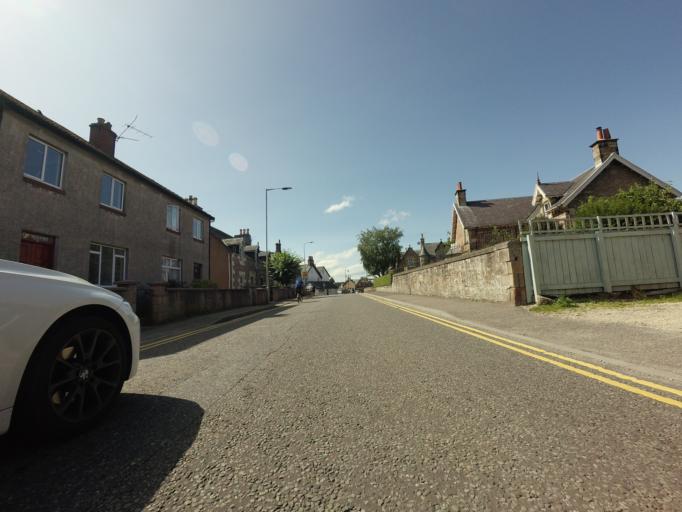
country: GB
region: Scotland
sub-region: Highland
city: Inverness
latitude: 57.4754
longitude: -4.2158
